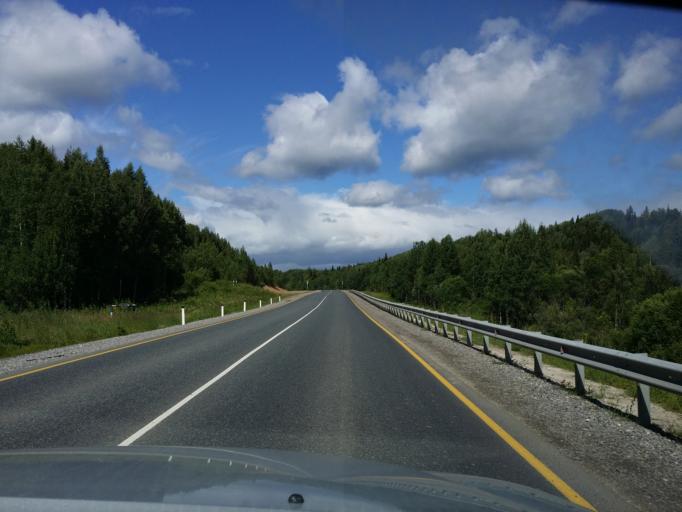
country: RU
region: Tjumen
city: Uvat
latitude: 59.1478
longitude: 68.9973
